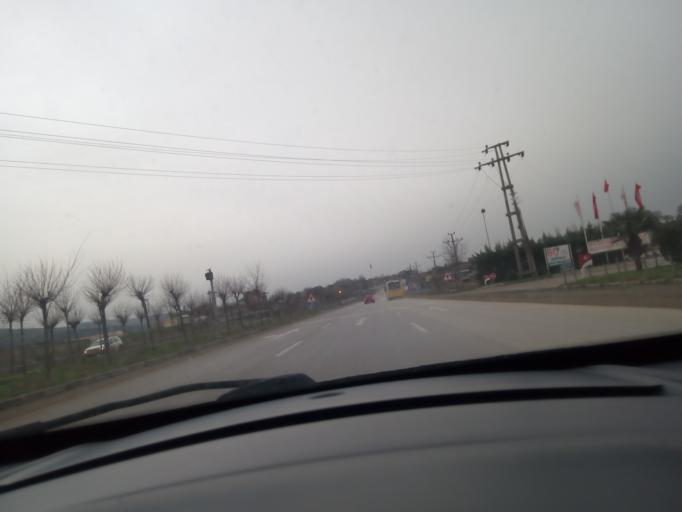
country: TR
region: Balikesir
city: Susurluk
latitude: 39.9544
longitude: 28.1709
